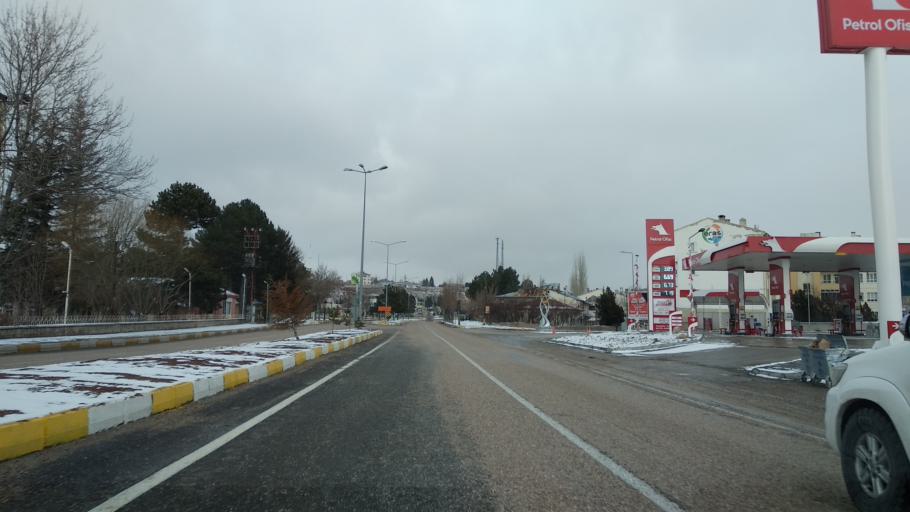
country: TR
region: Kayseri
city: Pinarbasi
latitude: 38.7194
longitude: 36.3853
